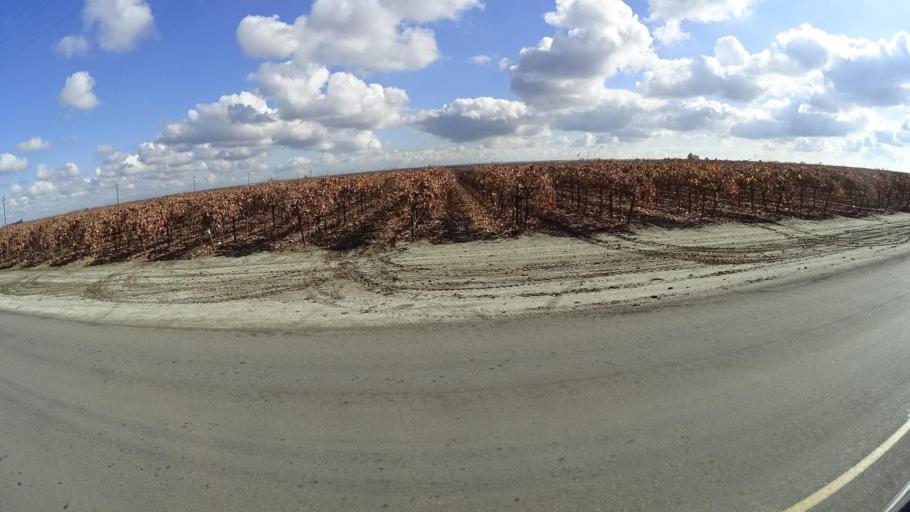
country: US
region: California
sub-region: Kern County
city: McFarland
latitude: 35.6517
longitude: -119.2322
